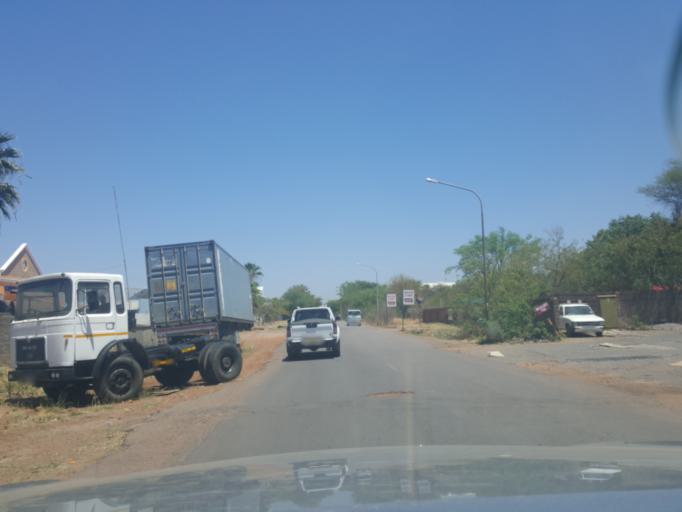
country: BW
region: South East
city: Gaborone
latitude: -24.6849
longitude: 25.8892
